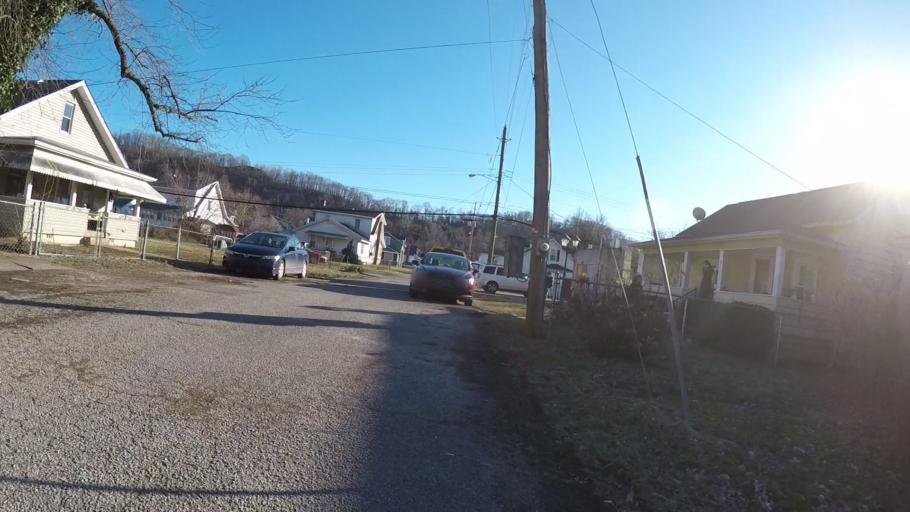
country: US
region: West Virginia
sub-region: Cabell County
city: Pea Ridge
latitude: 38.4306
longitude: -82.3786
